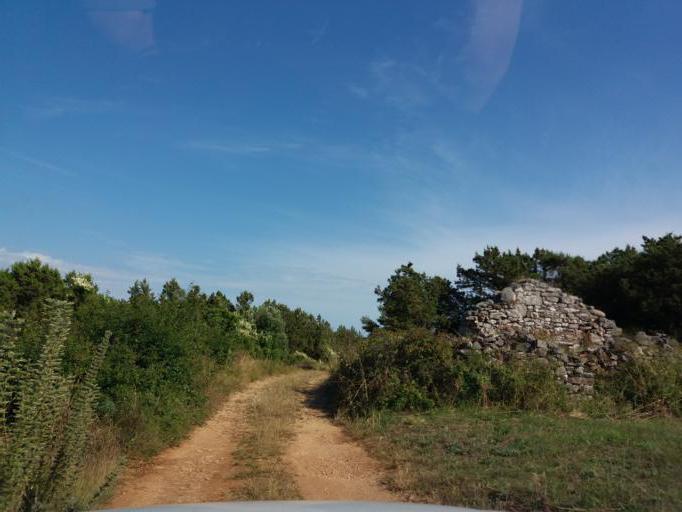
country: HR
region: Zadarska
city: Ugljan
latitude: 44.1327
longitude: 14.8617
